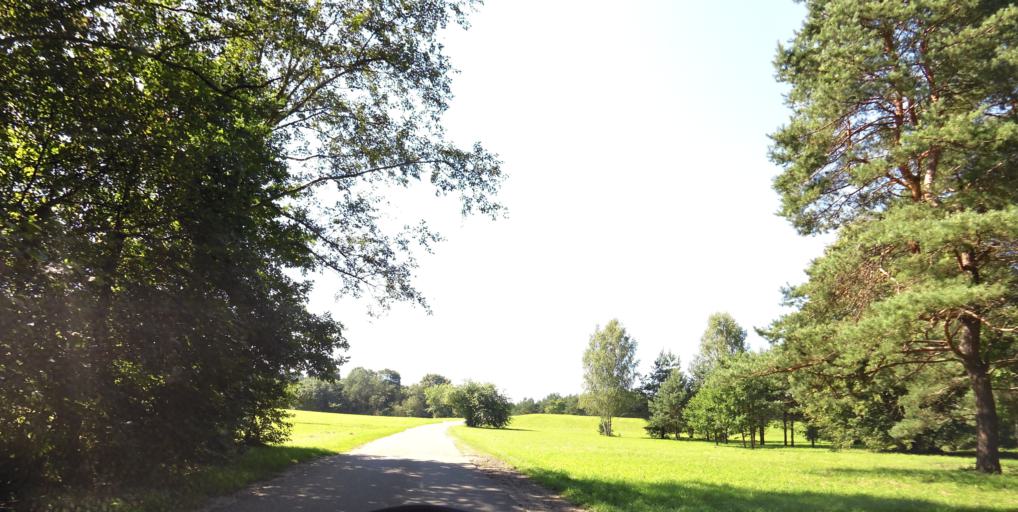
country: LT
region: Vilnius County
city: Rasos
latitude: 54.6882
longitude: 25.3669
